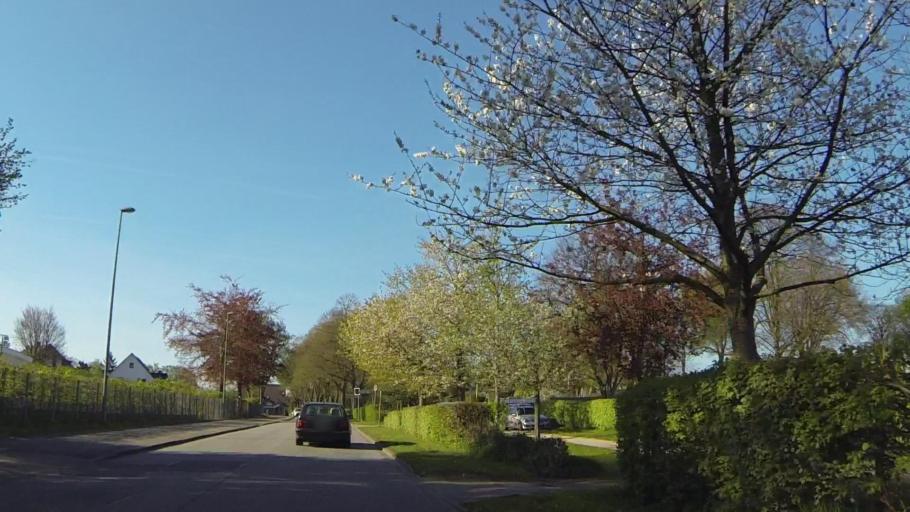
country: DE
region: Schleswig-Holstein
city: Wedel
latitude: 53.5880
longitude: 9.7108
